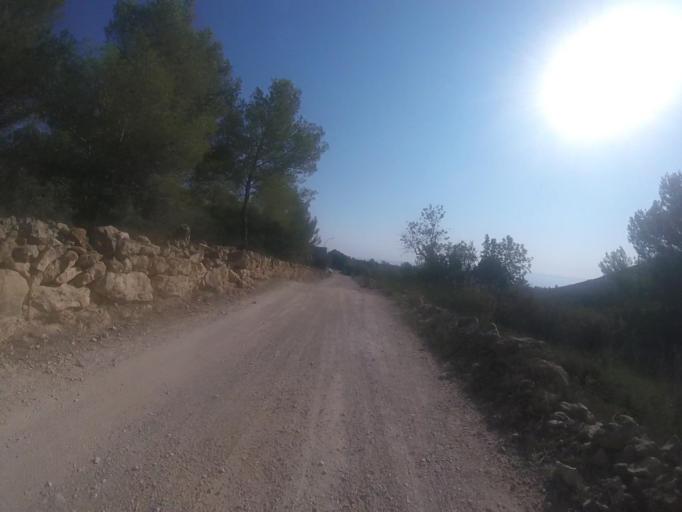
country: ES
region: Valencia
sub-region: Provincia de Castello
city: Peniscola
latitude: 40.3316
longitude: 0.3635
